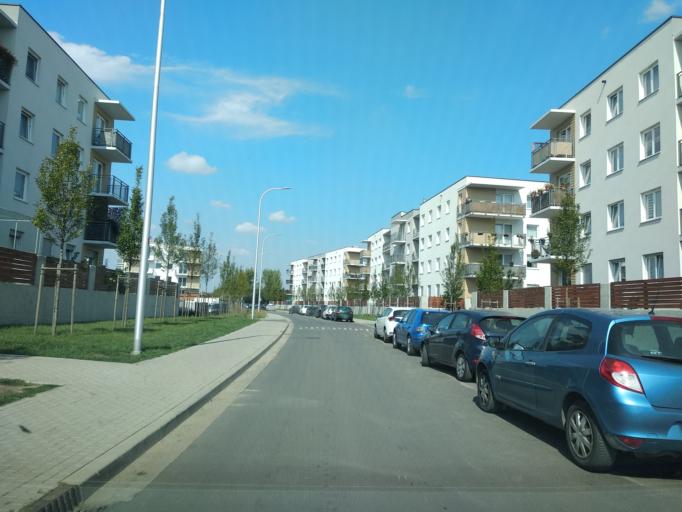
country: PL
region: Lower Silesian Voivodeship
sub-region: Powiat wroclawski
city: Zerniki Wroclawskie
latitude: 51.0541
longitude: 17.0547
